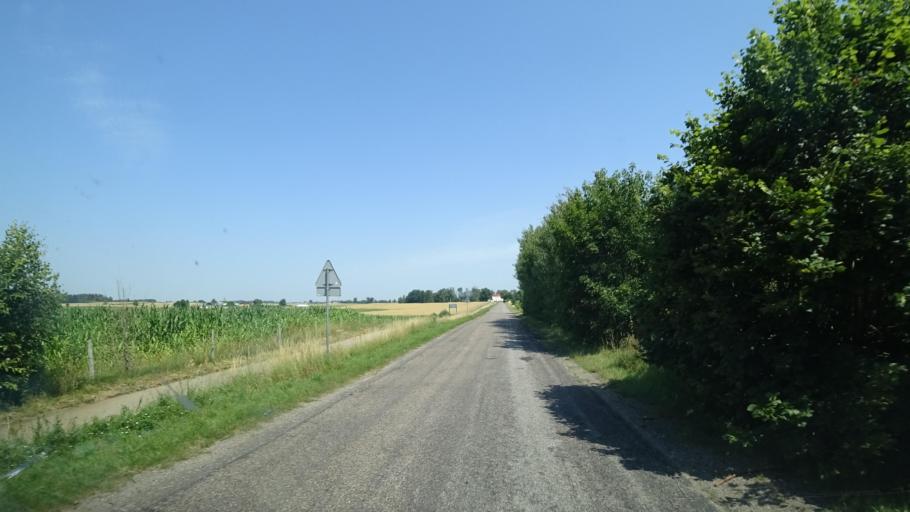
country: PL
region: Pomeranian Voivodeship
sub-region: Powiat chojnicki
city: Brusy
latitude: 53.8760
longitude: 17.6284
